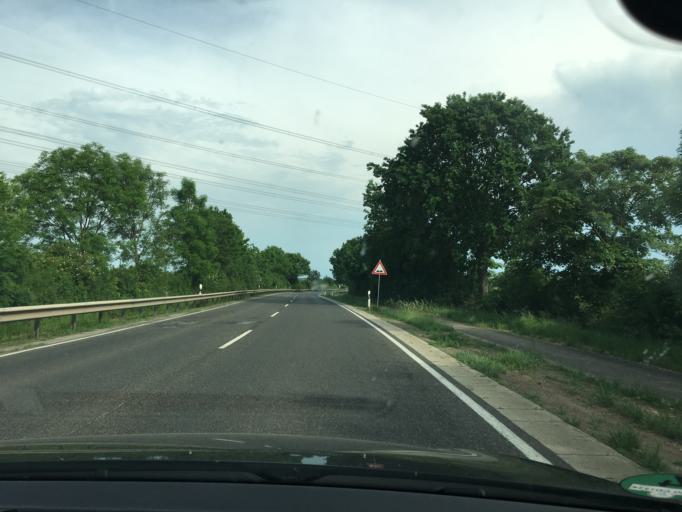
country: DE
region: North Rhine-Westphalia
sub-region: Regierungsbezirk Koln
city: Kreuzau
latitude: 50.7534
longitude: 6.5341
